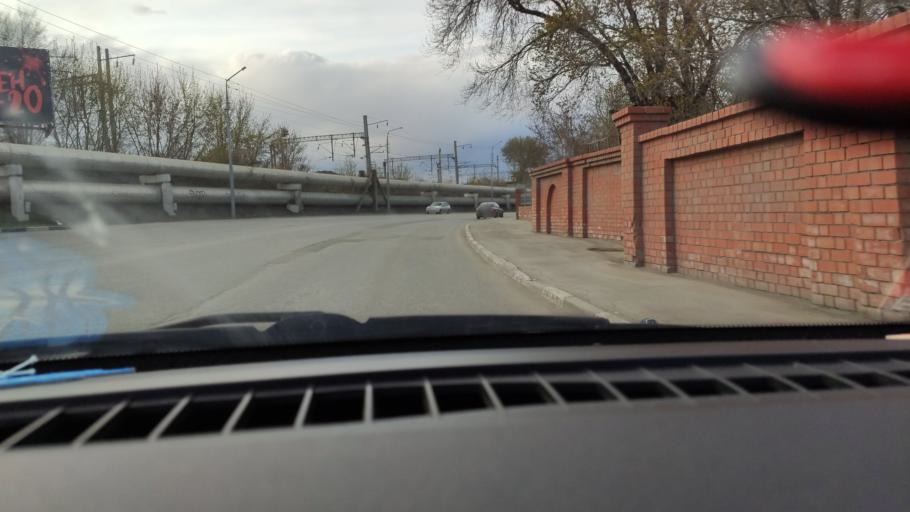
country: RU
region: Saratov
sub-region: Saratovskiy Rayon
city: Saratov
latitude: 51.5636
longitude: 46.0032
